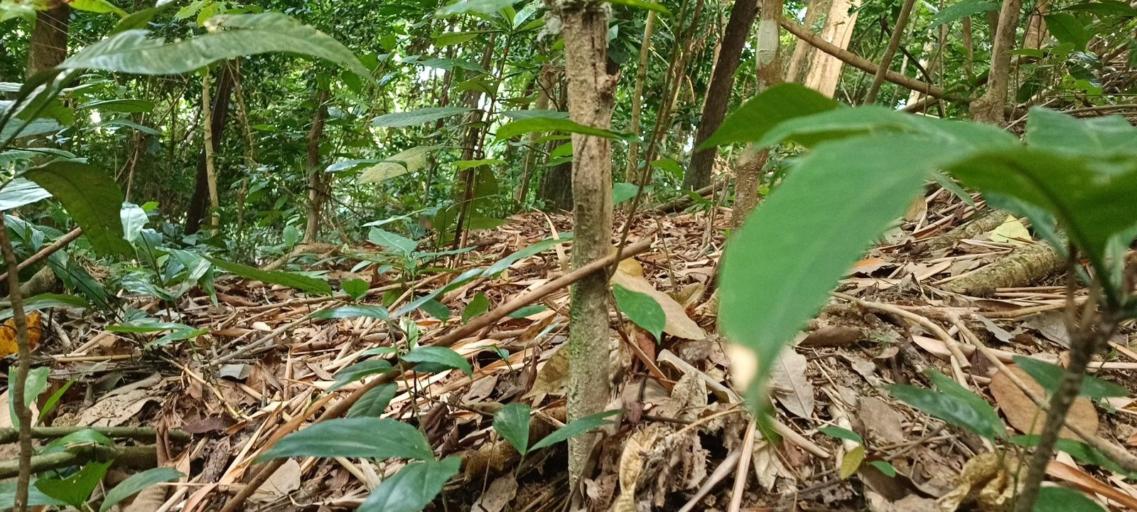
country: MY
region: Penang
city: Kampung Sungai Ara
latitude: 5.3490
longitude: 100.2821
